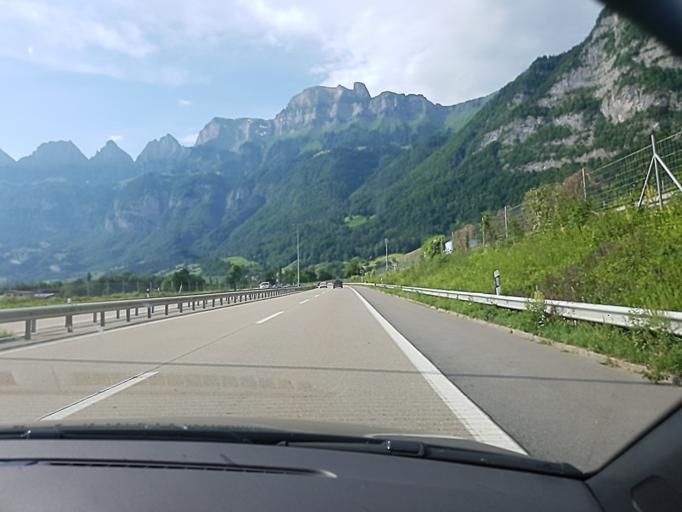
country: CH
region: Saint Gallen
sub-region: Wahlkreis Sarganserland
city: Flums
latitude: 47.1069
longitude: 9.3430
